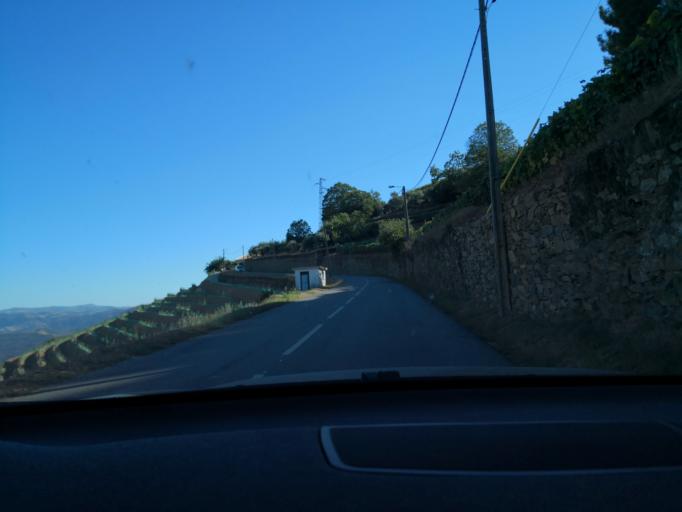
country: PT
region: Vila Real
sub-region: Sabrosa
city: Vilela
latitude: 41.2228
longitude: -7.5626
